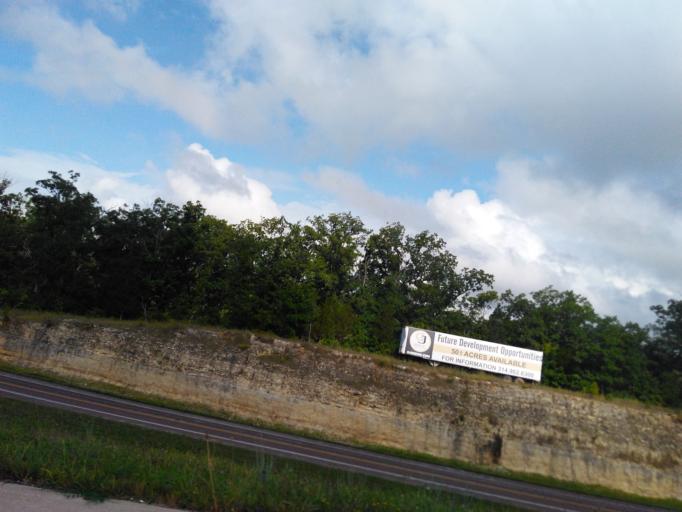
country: US
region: Missouri
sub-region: Jefferson County
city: Hillsboro
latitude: 38.2543
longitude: -90.5565
